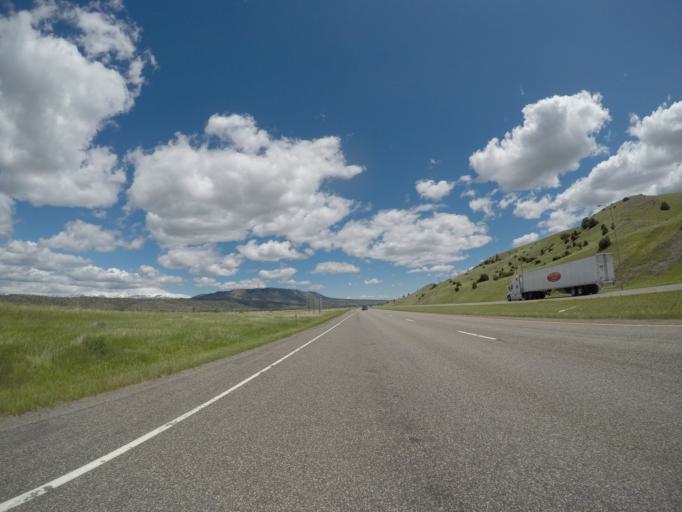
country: US
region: Montana
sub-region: Park County
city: Livingston
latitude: 45.7085
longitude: -110.4510
